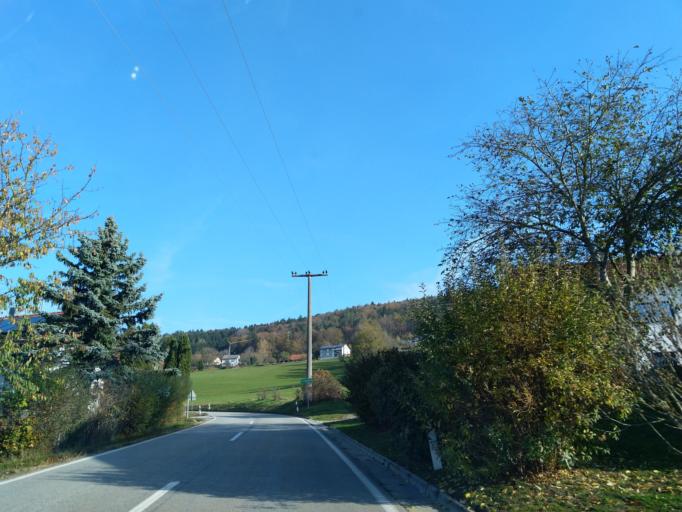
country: DE
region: Bavaria
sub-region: Lower Bavaria
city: Lalling
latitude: 48.8545
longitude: 13.1404
